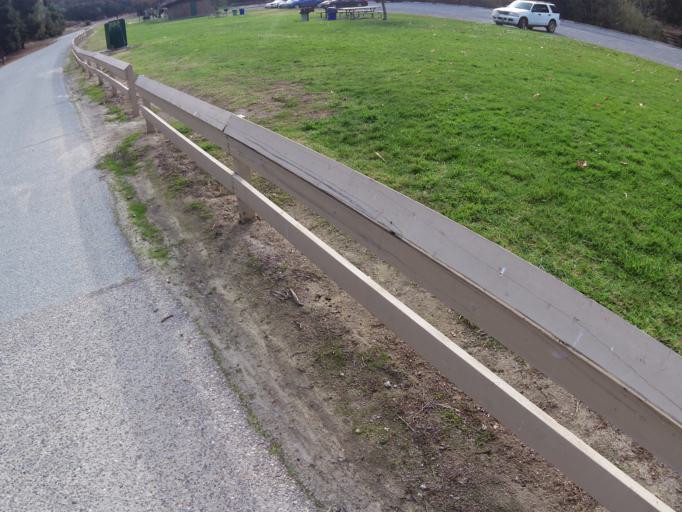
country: US
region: California
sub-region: Monterey County
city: Salinas
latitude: 36.5978
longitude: -121.6921
